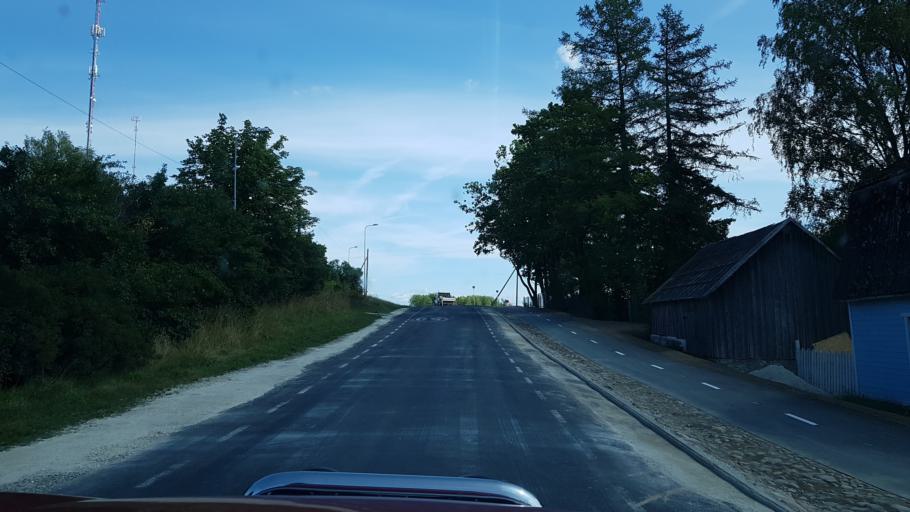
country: EE
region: Jaervamaa
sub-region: Jaerva-Jaani vald
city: Jarva-Jaani
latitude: 59.0387
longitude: 25.8875
